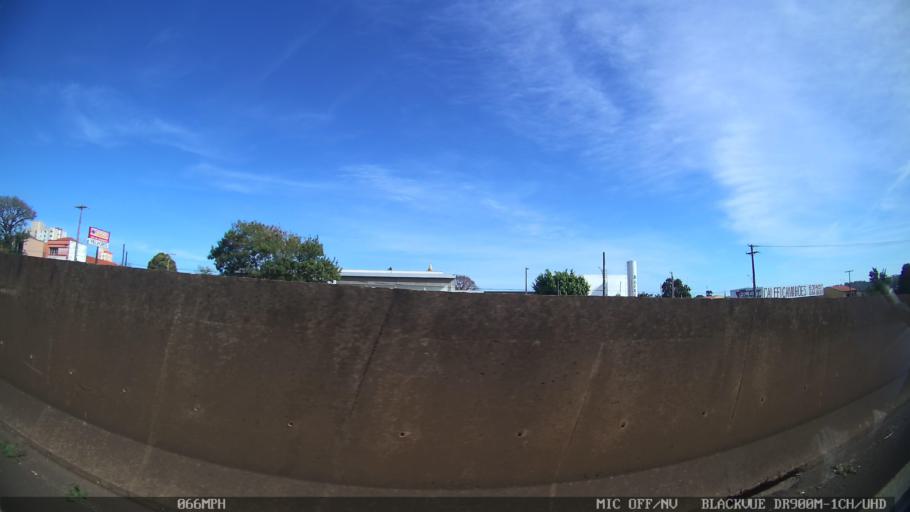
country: BR
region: Sao Paulo
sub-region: Araras
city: Araras
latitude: -22.3522
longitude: -47.3946
